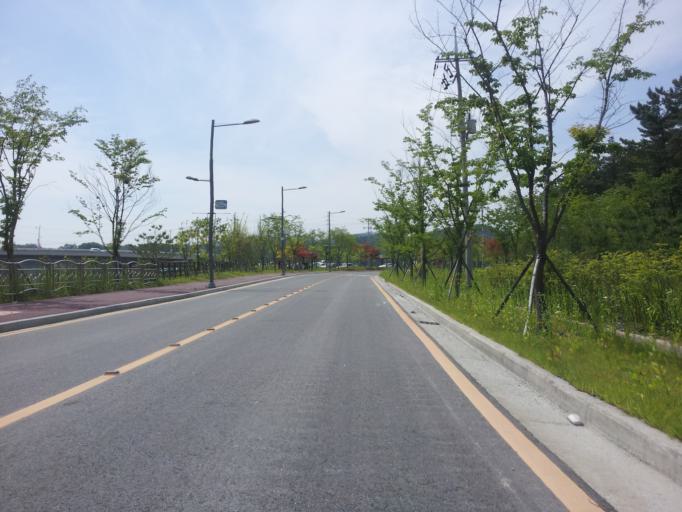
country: KR
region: Daejeon
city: Sintansin
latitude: 36.4578
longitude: 127.4671
